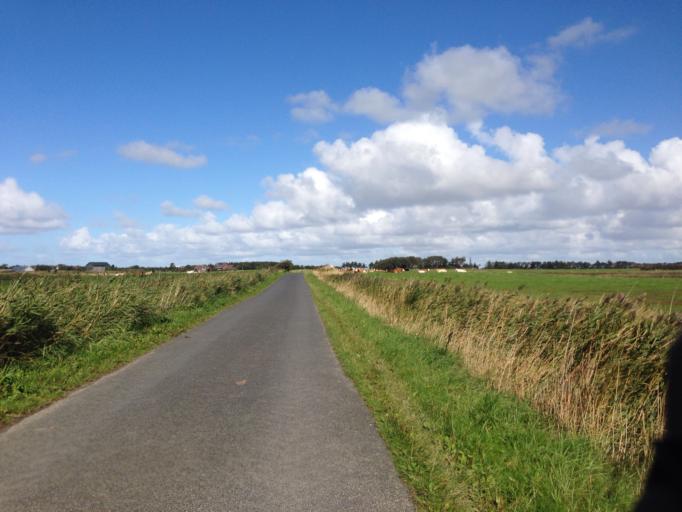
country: DE
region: Schleswig-Holstein
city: Witsum
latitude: 54.6979
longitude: 8.4268
